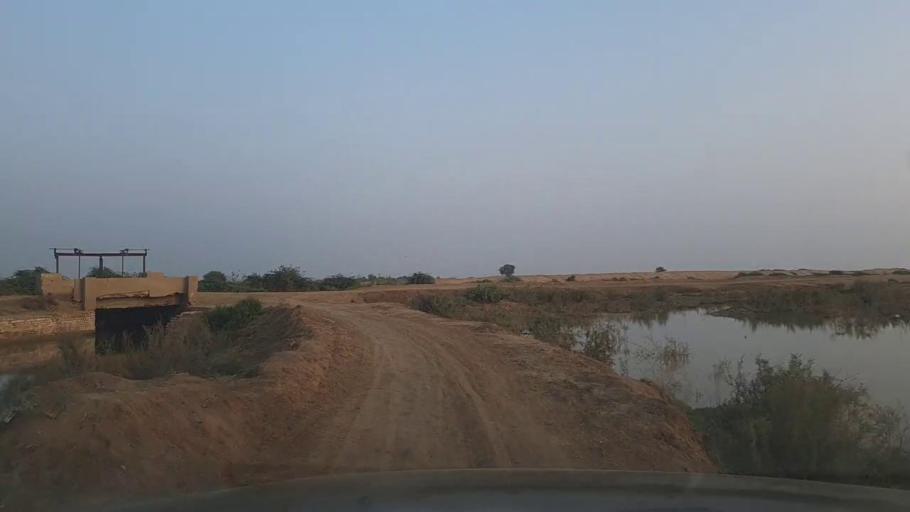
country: PK
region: Sindh
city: Jati
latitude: 24.5364
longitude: 68.4080
